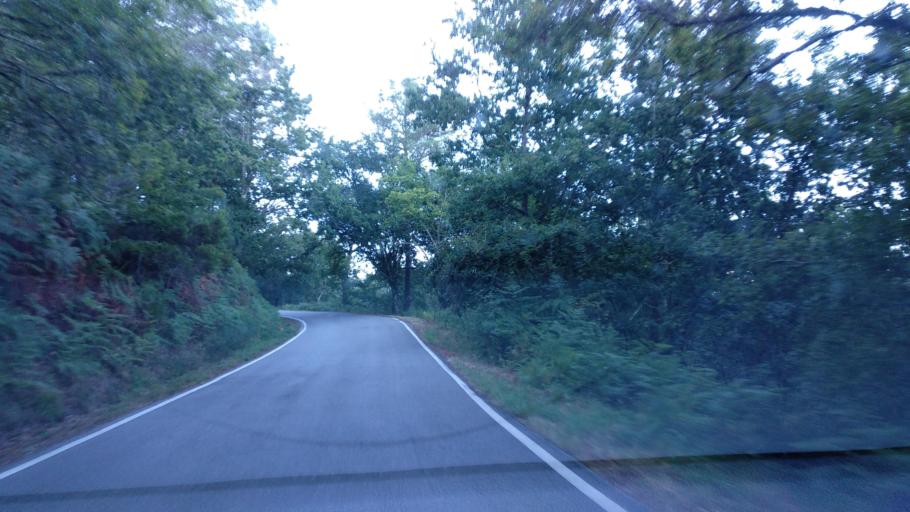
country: ES
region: Galicia
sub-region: Provincia de Pontevedra
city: Fornelos de Montes
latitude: 42.3509
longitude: -8.4899
